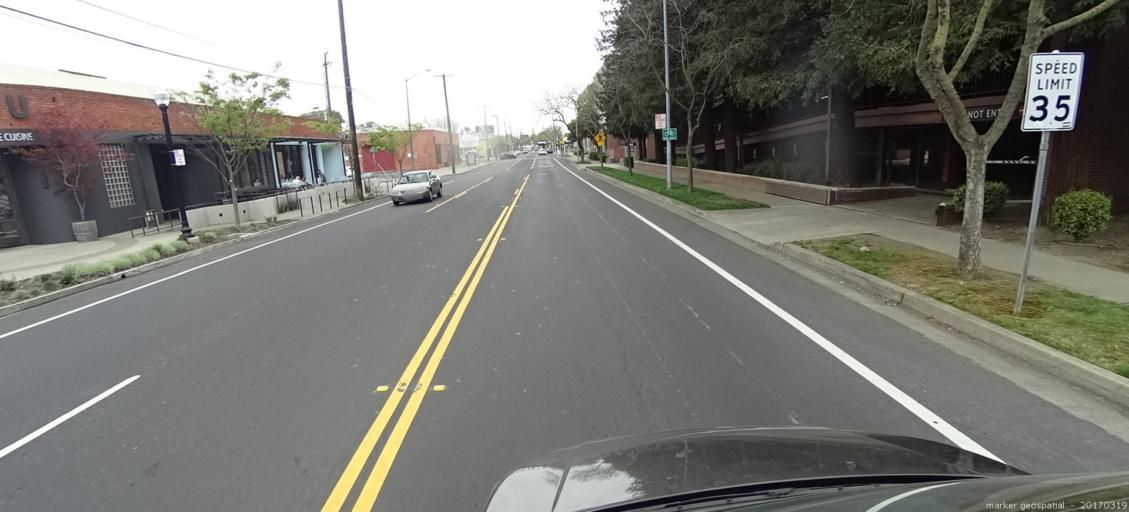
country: US
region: California
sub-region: Sacramento County
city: Sacramento
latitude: 38.5691
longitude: -121.4663
